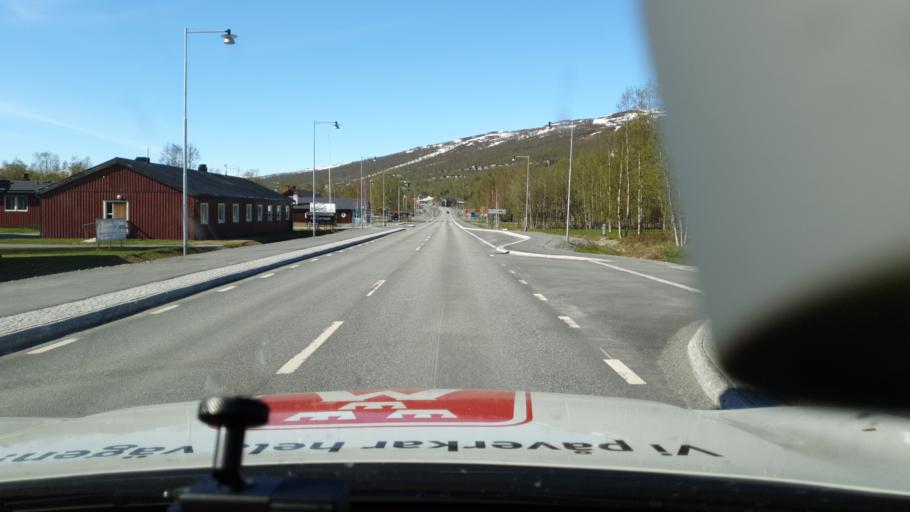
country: NO
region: Nordland
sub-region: Rana
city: Mo i Rana
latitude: 65.8115
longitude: 15.0885
